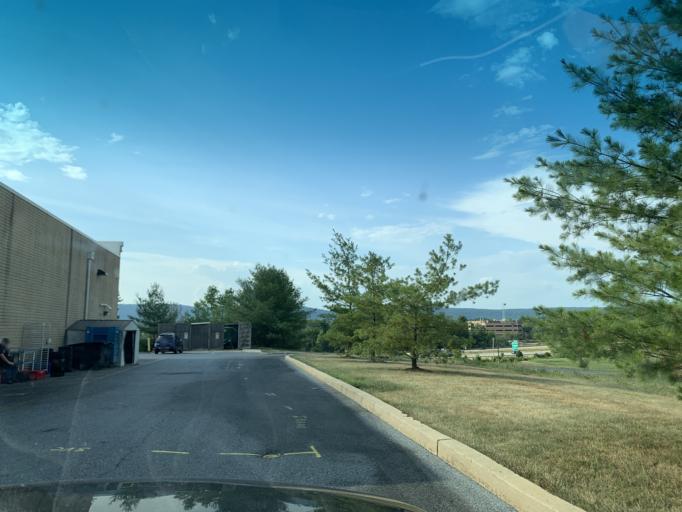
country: US
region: Pennsylvania
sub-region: Dauphin County
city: Progress
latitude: 40.3035
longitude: -76.8425
